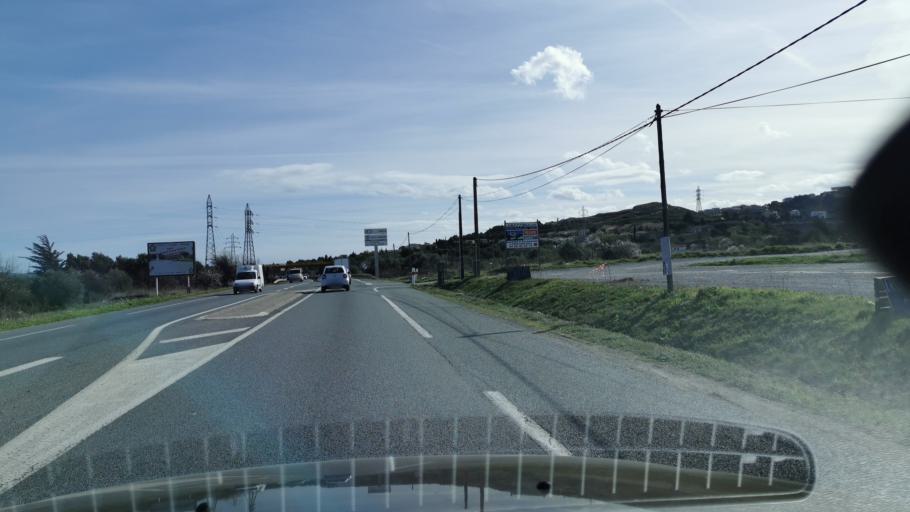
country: FR
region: Languedoc-Roussillon
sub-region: Departement de l'Aude
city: Narbonne
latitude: 43.1741
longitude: 2.9749
